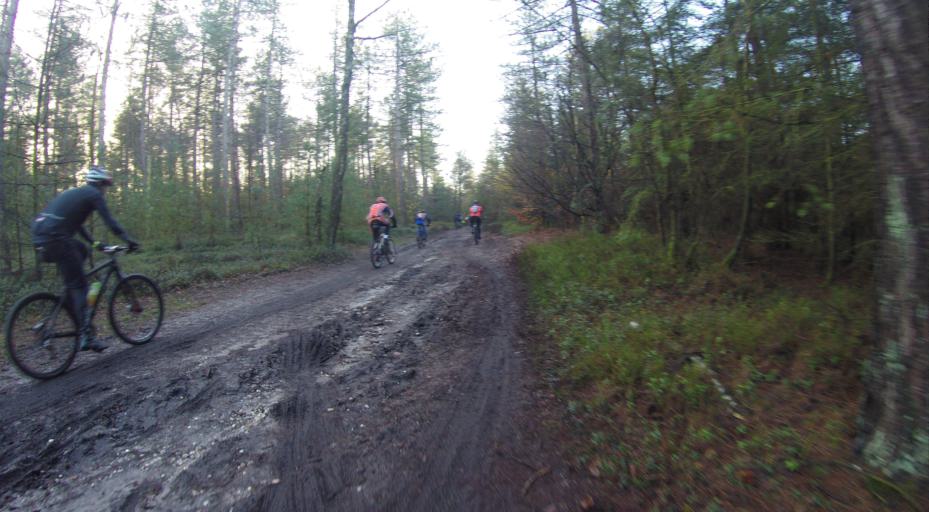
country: NL
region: Overijssel
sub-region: Gemeente Hof van Twente
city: Markelo
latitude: 52.3125
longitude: 6.4171
